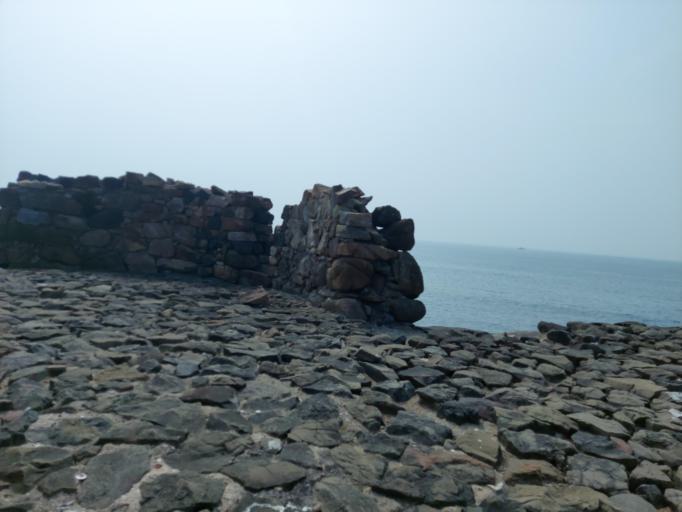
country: IN
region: Maharashtra
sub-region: Sindhudurg
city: Malvan
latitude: 16.0394
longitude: 73.4610
